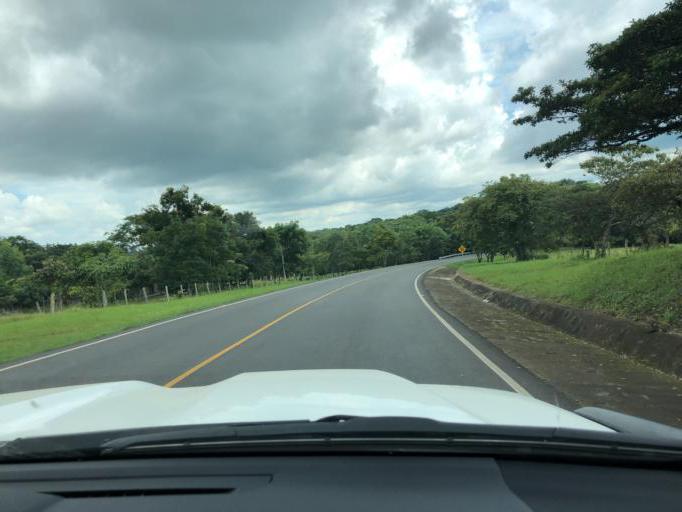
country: NI
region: Chontales
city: Santo Tomas
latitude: 12.0622
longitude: -85.0560
